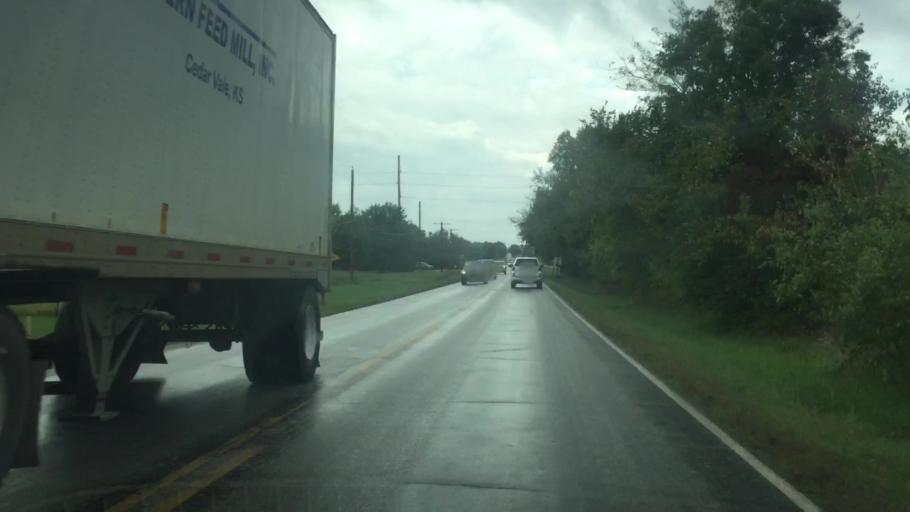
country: US
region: Kansas
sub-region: Allen County
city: Iola
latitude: 37.8946
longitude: -95.4095
